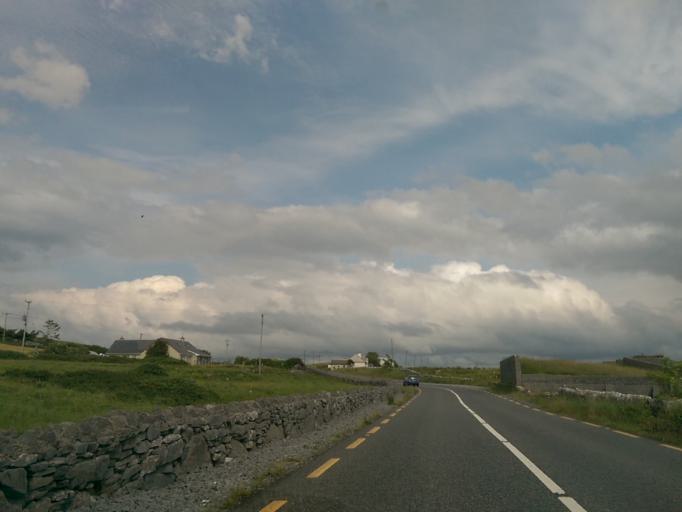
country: IE
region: Connaught
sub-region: County Galway
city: Bearna
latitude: 53.0405
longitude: -9.2695
